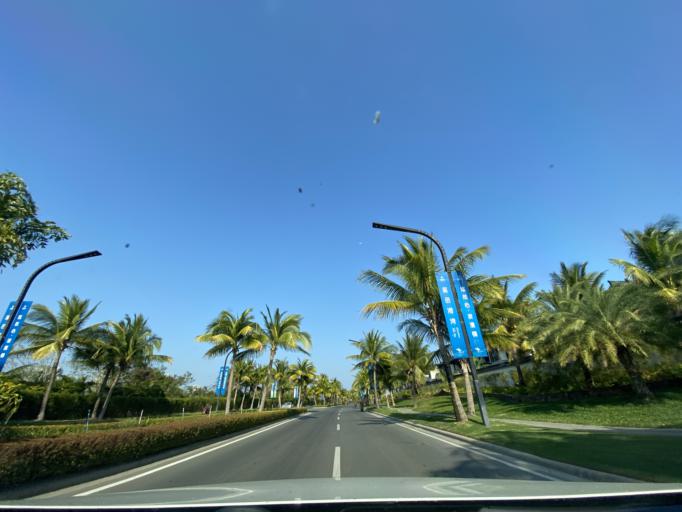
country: CN
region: Hainan
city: Xincun
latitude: 18.4226
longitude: 109.9504
